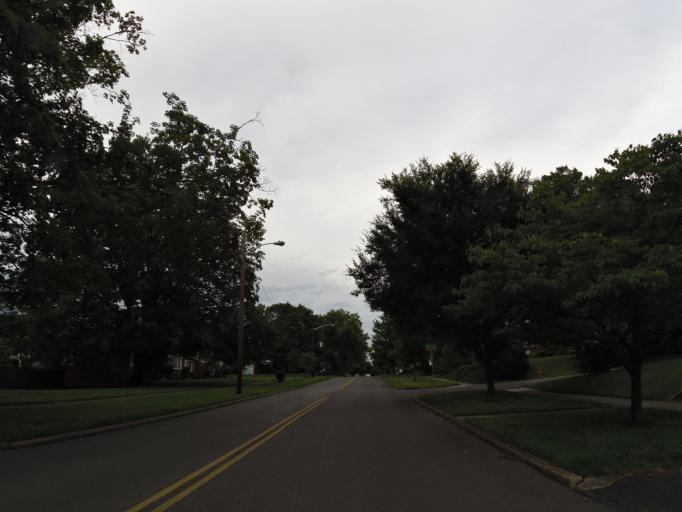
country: US
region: Tennessee
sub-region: Knox County
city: Knoxville
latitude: 36.0045
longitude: -83.9241
